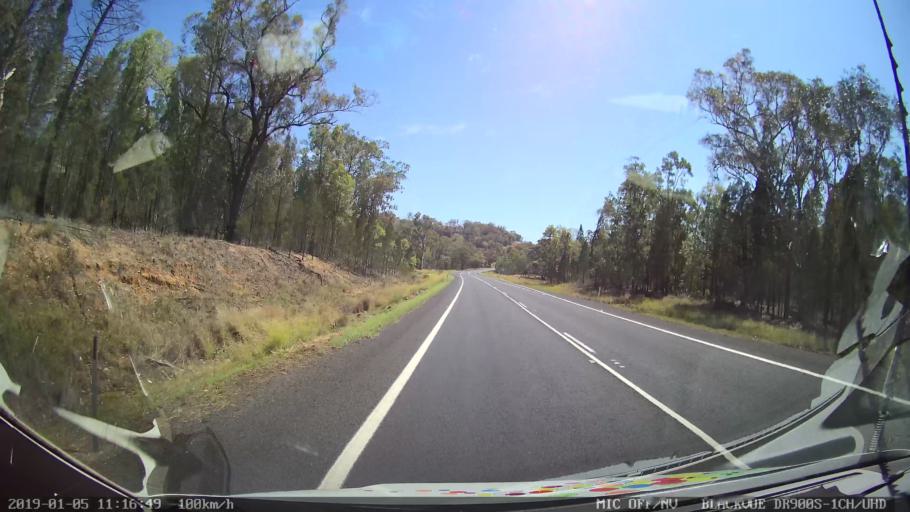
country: AU
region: New South Wales
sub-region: Warrumbungle Shire
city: Coonabarabran
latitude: -31.3338
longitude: 149.3011
